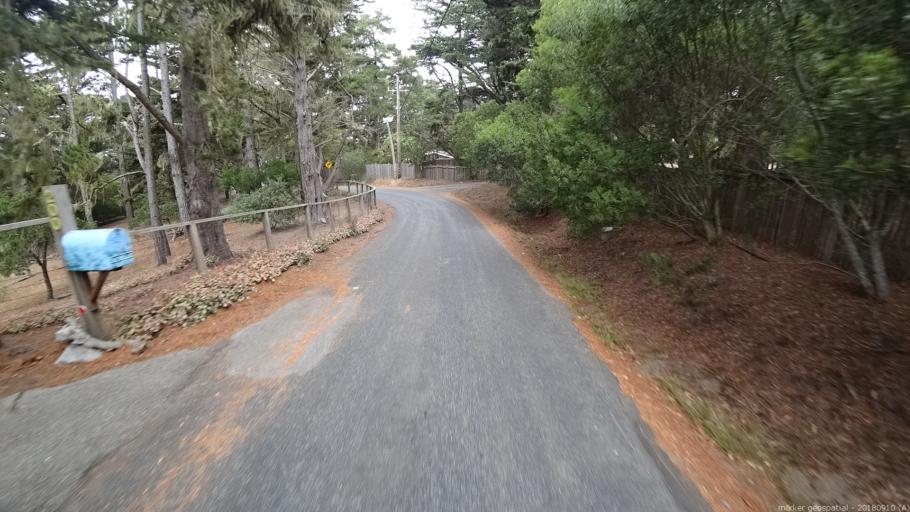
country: US
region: California
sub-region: Monterey County
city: Carmel-by-the-Sea
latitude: 36.4906
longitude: -121.9354
